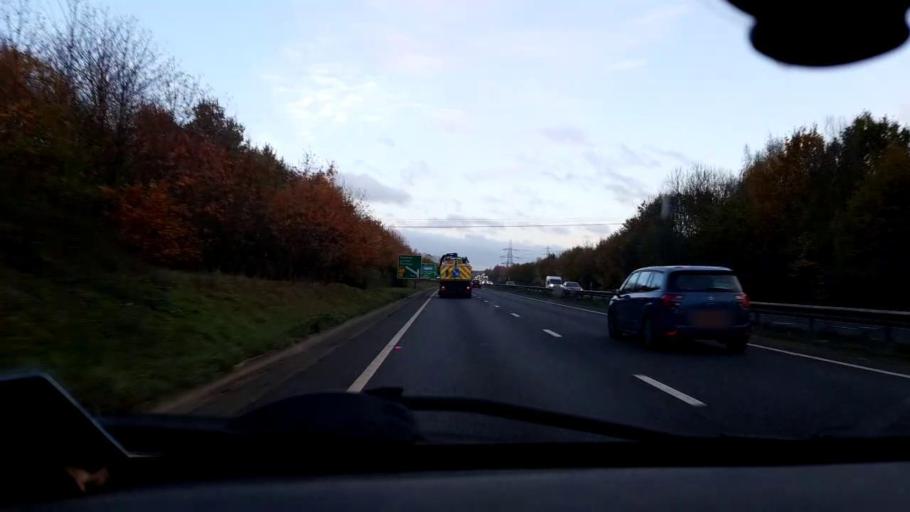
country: GB
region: England
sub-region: Norfolk
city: Bowthorpe
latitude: 52.6149
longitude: 1.2125
